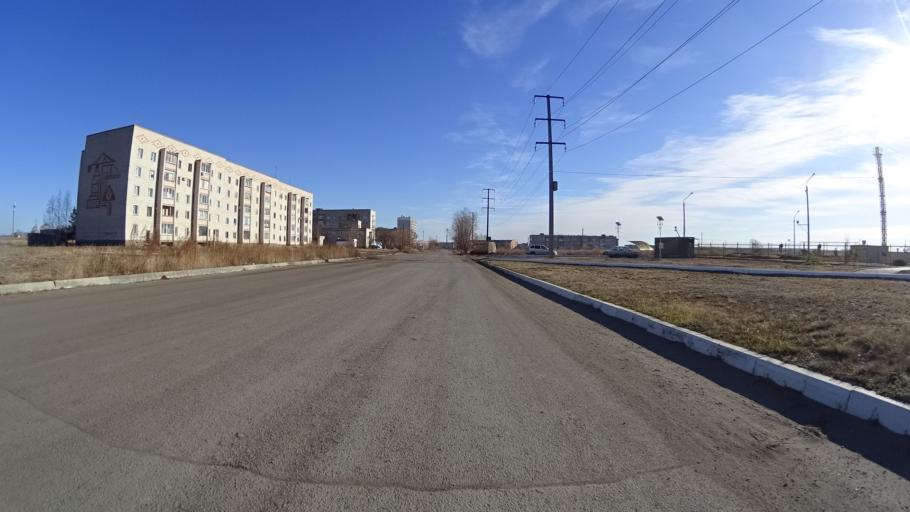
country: RU
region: Chelyabinsk
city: Troitsk
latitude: 54.0780
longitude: 61.5206
